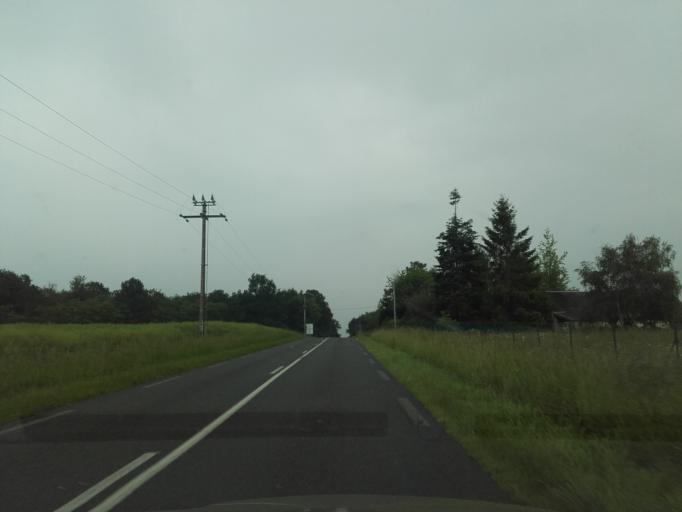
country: FR
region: Centre
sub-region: Departement d'Indre-et-Loire
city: Beaumont-la-Ronce
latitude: 47.6099
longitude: 0.6604
